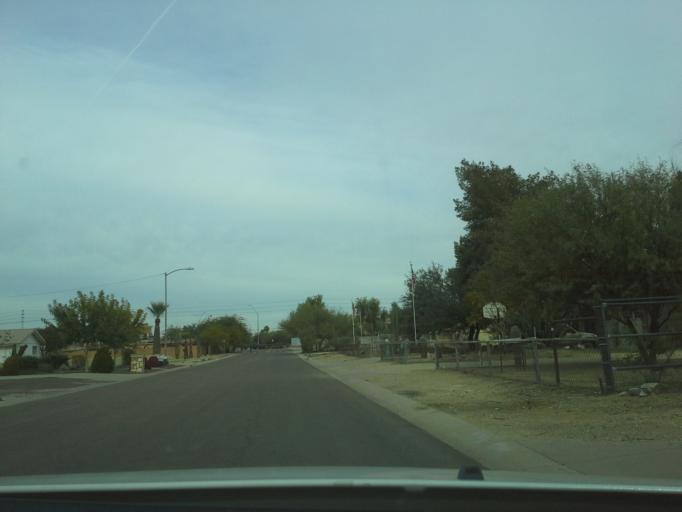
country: US
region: Arizona
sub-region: Maricopa County
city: Paradise Valley
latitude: 33.6248
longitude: -112.0242
